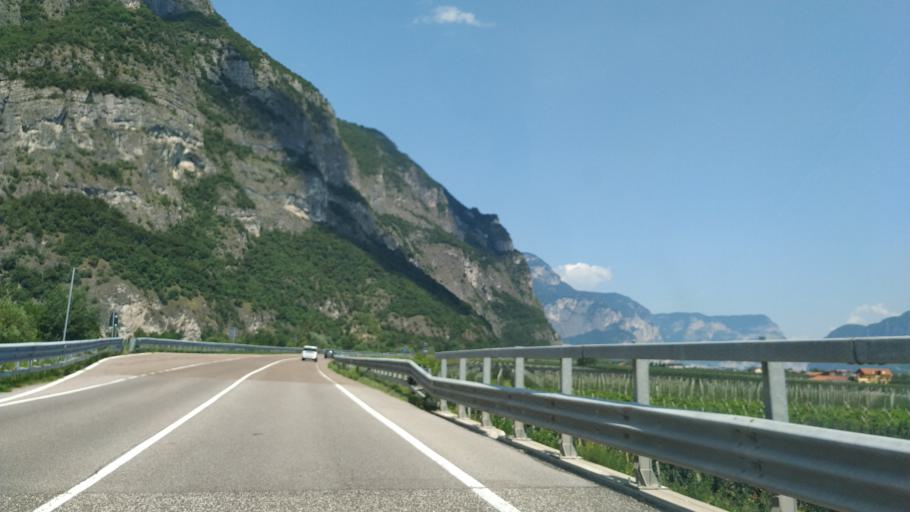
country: IT
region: Trentino-Alto Adige
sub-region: Provincia di Trento
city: Zambana
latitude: 46.1591
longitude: 11.0793
